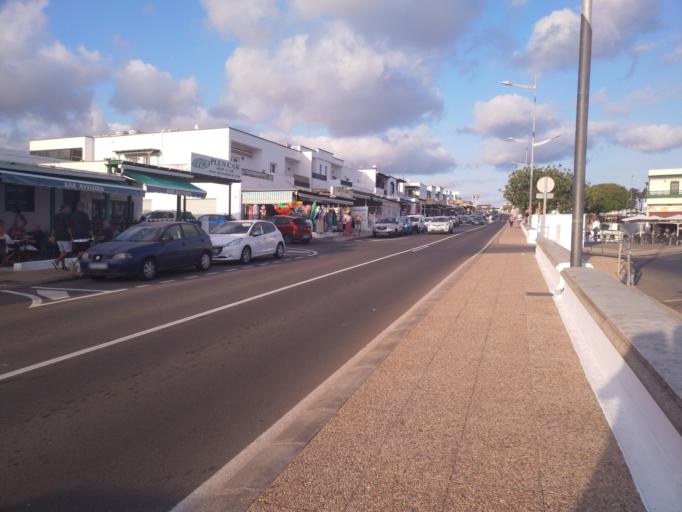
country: ES
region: Canary Islands
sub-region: Provincia de Las Palmas
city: Playa Blanca
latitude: 28.8633
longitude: -13.8290
